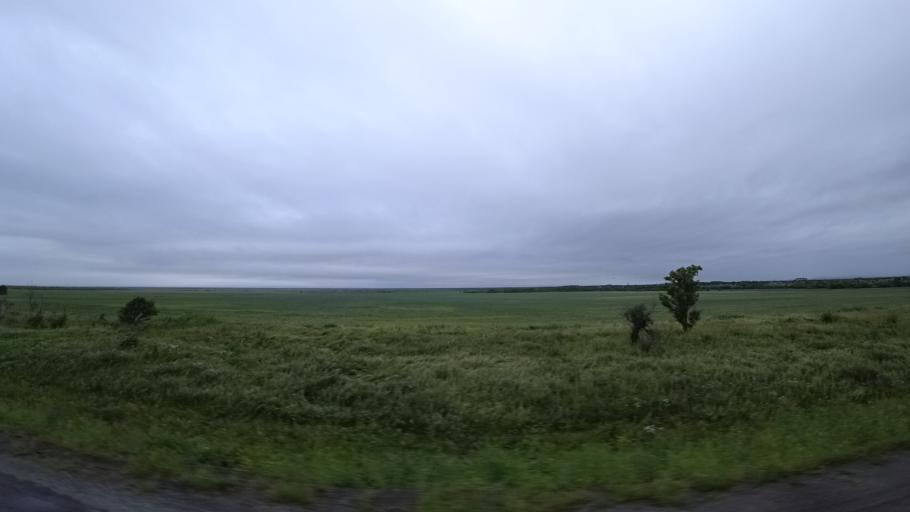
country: RU
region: Primorskiy
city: Chernigovka
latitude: 44.3042
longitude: 132.5355
